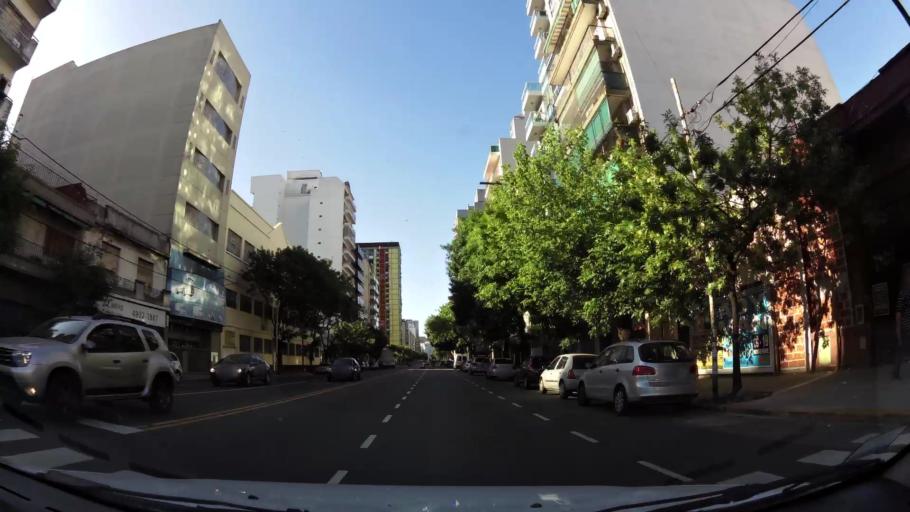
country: AR
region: Buenos Aires F.D.
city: Buenos Aires
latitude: -34.6235
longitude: -58.4275
